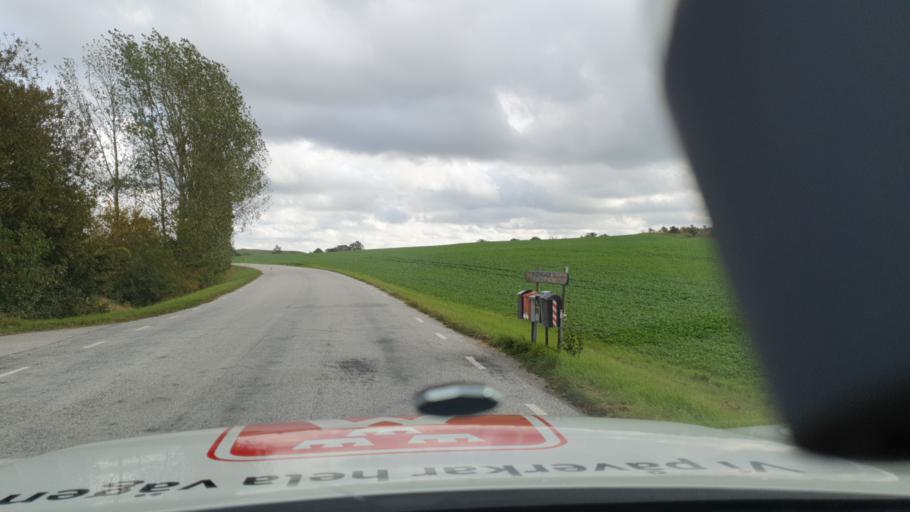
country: SE
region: Skane
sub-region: Malmo
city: Oxie
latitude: 55.5142
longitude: 13.1034
